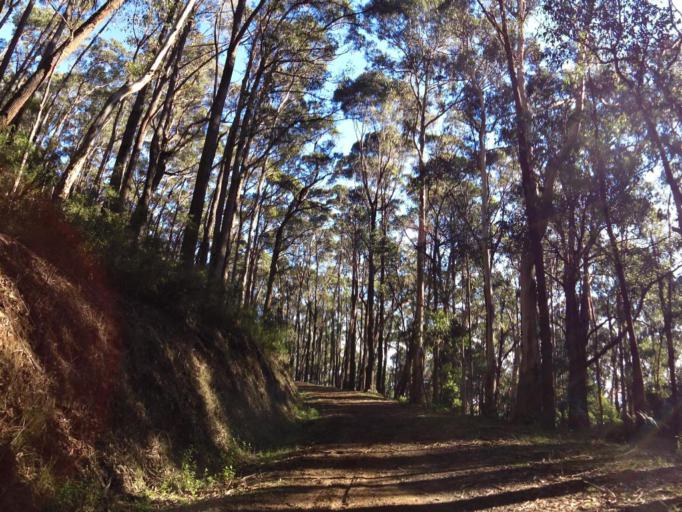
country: AU
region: Victoria
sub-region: Yarra Ranges
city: Millgrove
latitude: -37.7696
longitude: 145.6608
